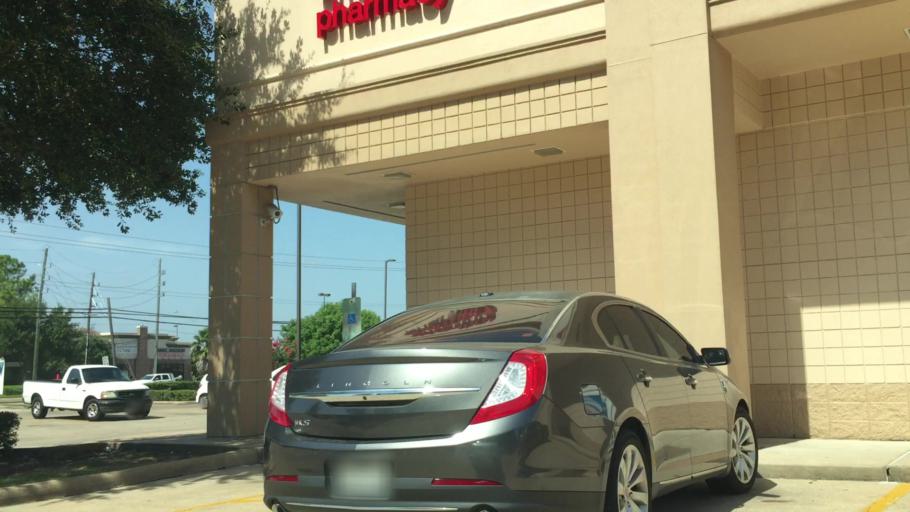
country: US
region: Texas
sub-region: Harris County
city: Bunker Hill Village
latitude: 29.7372
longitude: -95.5814
